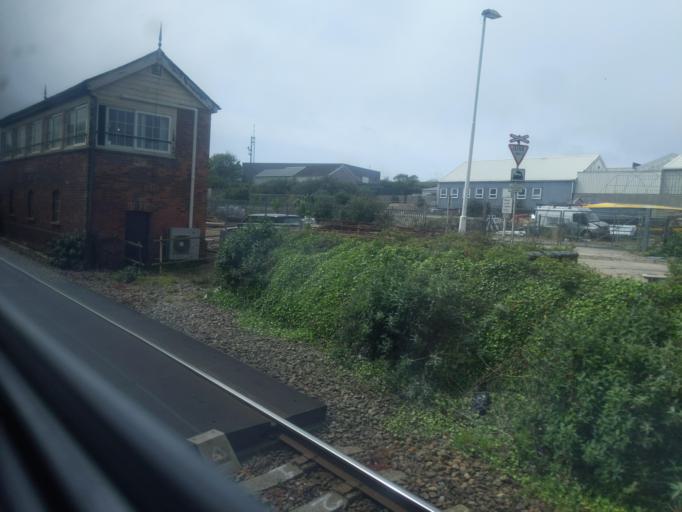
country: GB
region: England
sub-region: Cornwall
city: Hayle
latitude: 50.1715
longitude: -5.4414
